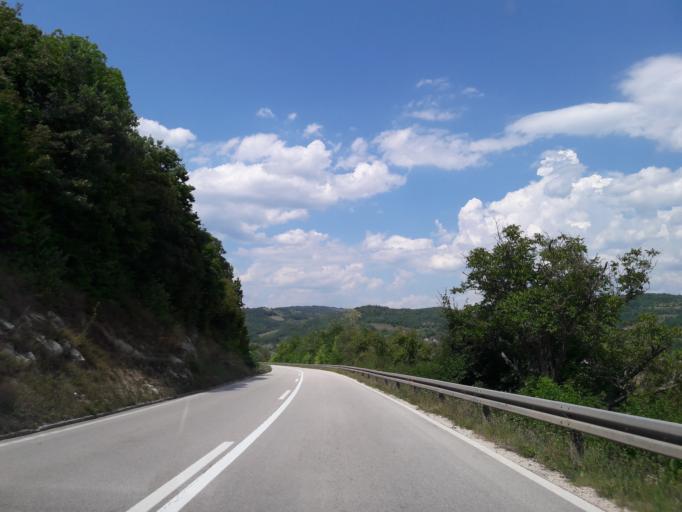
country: BA
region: Republika Srpska
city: Mrkonjic Grad
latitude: 44.5234
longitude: 17.1510
